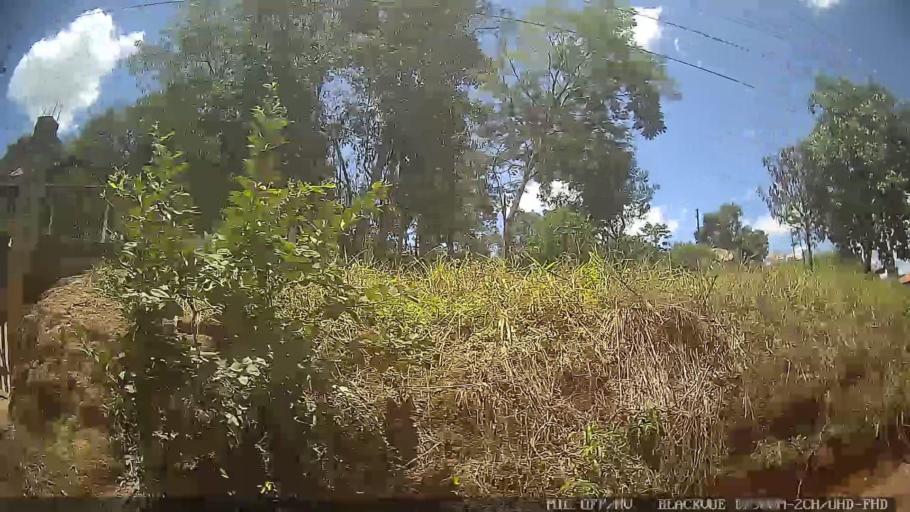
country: BR
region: Sao Paulo
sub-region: Piracaia
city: Piracaia
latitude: -23.0192
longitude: -46.4566
